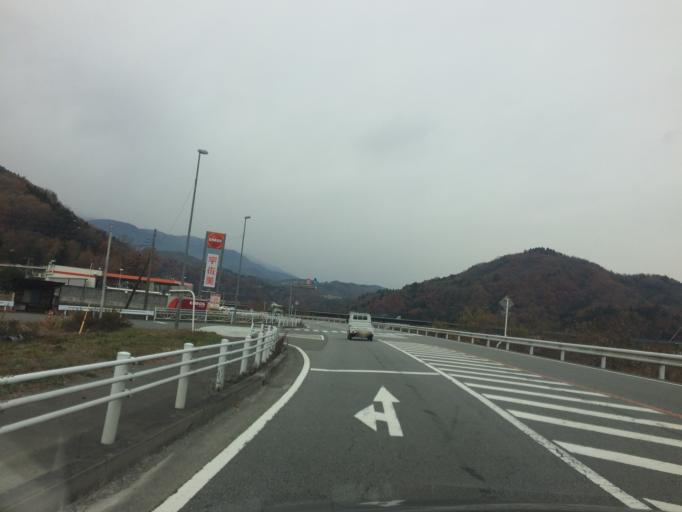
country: JP
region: Yamanashi
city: Ryuo
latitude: 35.4533
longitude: 138.4465
